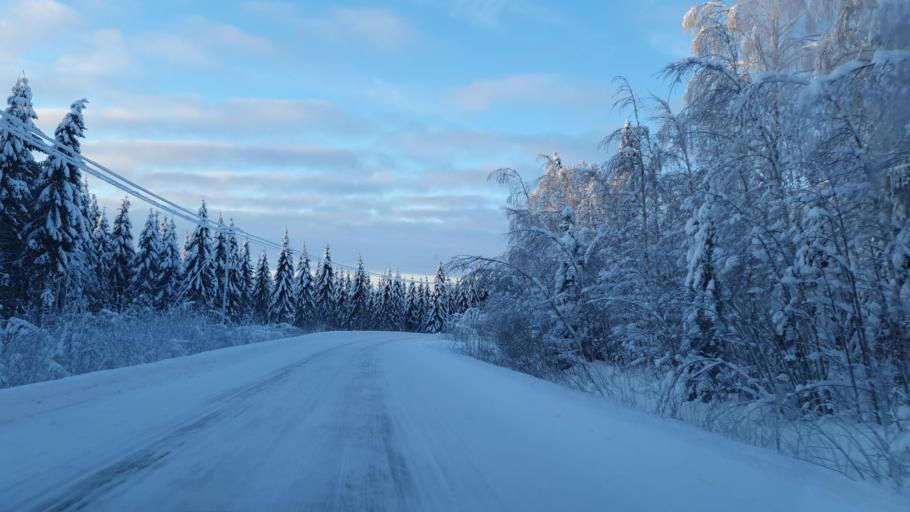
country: FI
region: Kainuu
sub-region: Kajaani
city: Ristijaervi
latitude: 64.3376
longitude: 28.0639
